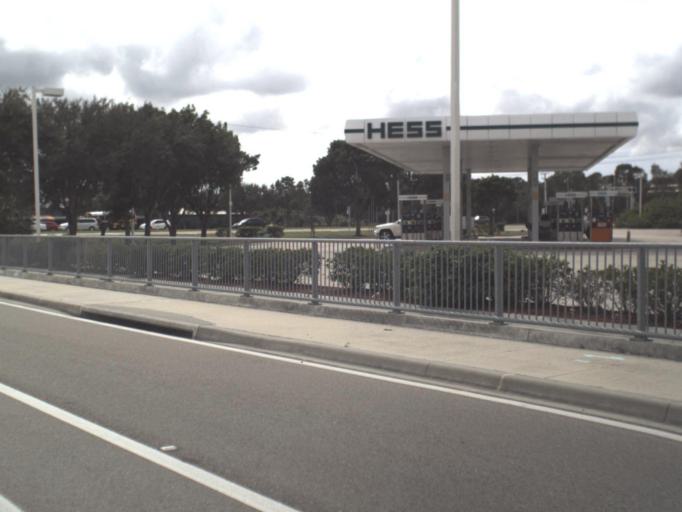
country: US
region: Florida
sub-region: Lee County
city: Villas
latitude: 26.5293
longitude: -81.8528
